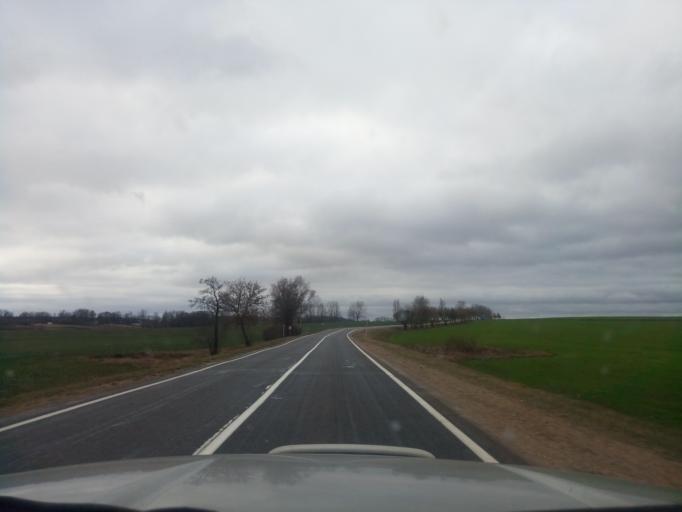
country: BY
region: Minsk
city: Kapyl'
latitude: 53.1857
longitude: 27.1808
